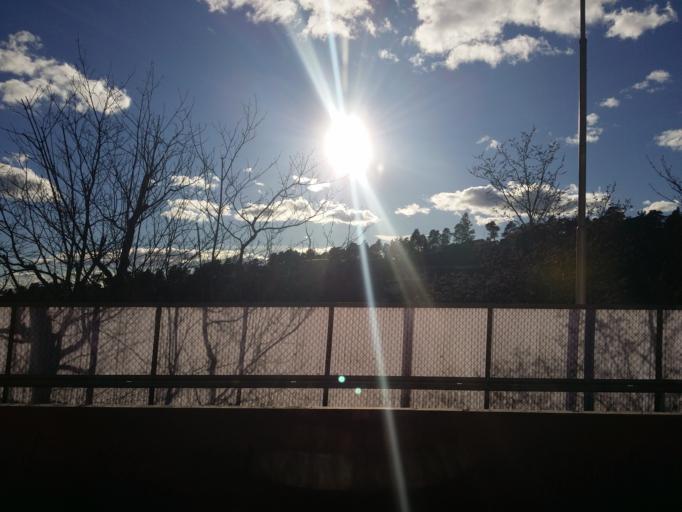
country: NO
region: Oslo
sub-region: Oslo
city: Oslo
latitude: 59.8717
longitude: 10.7801
